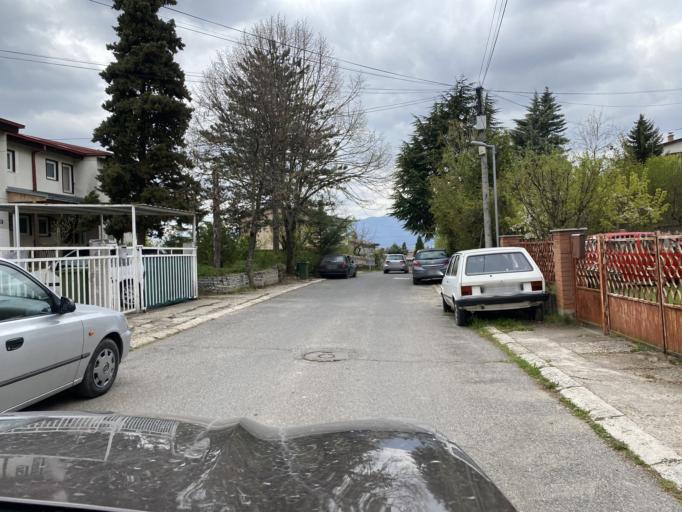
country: MK
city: Radishani
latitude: 42.0606
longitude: 21.4496
